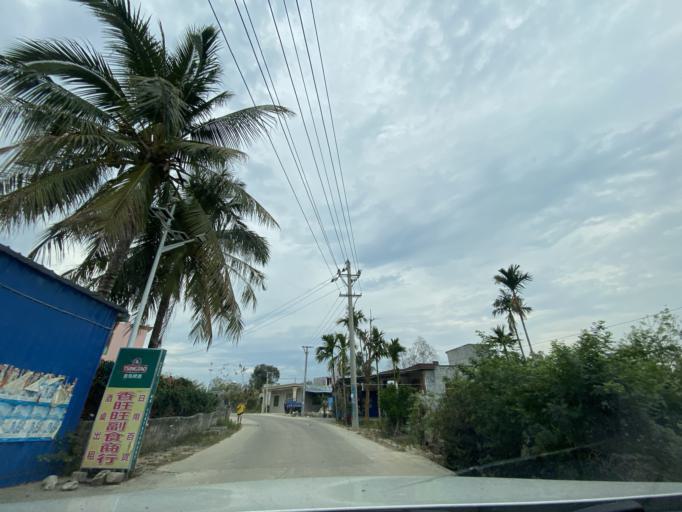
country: CN
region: Hainan
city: Yingzhou
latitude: 18.4167
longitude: 109.8230
